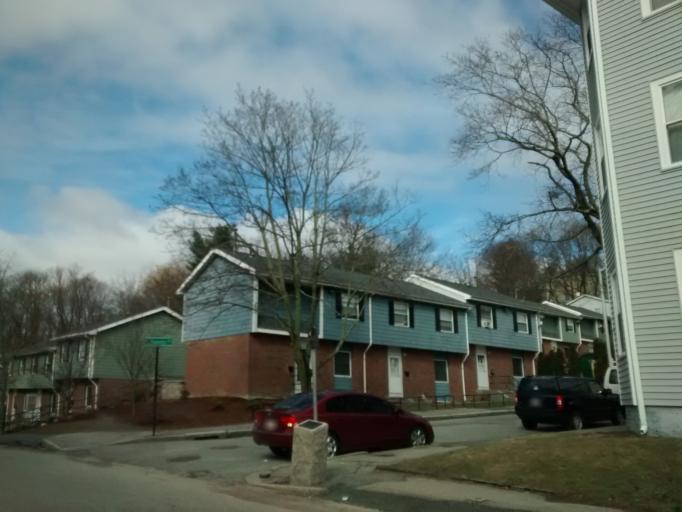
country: US
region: Massachusetts
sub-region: Worcester County
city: Worcester
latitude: 42.2828
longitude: -71.8002
